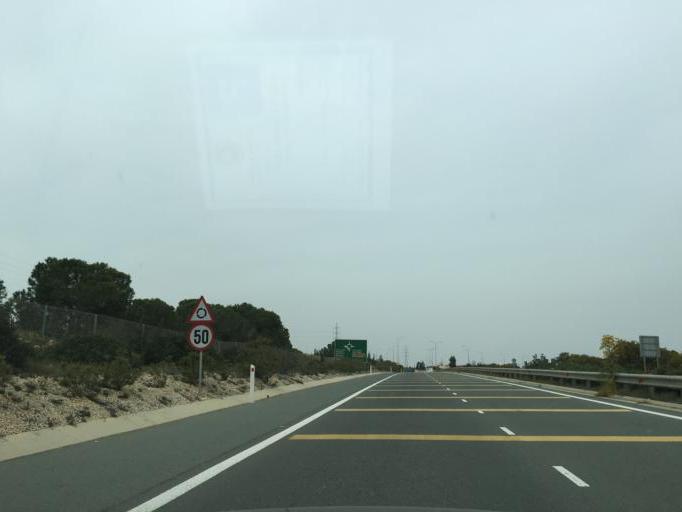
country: CY
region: Ammochostos
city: Ayia Napa
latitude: 35.0023
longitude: 33.9945
